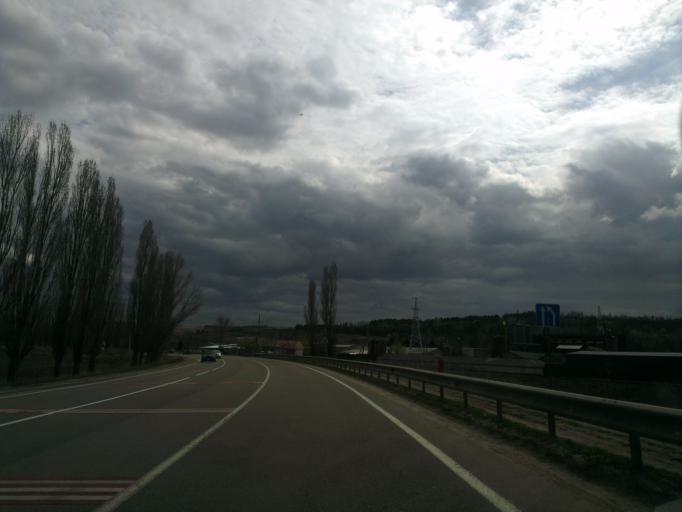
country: MD
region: Laloveni
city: Ialoveni
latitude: 46.9110
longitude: 28.6880
